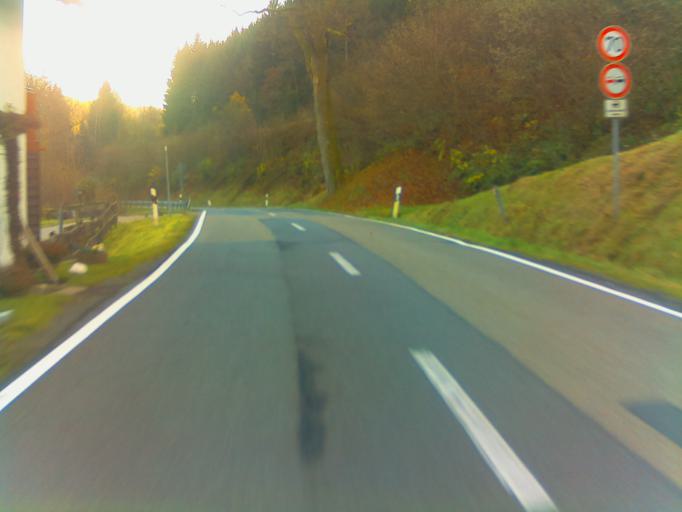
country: DE
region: Hesse
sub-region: Regierungsbezirk Darmstadt
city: Hesseneck
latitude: 49.5585
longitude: 9.0757
